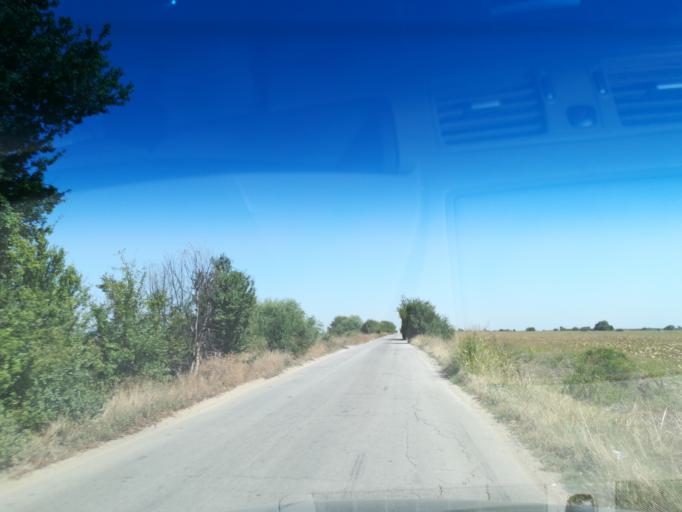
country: BG
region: Plovdiv
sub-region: Obshtina Suedinenie
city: Suedinenie
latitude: 42.2514
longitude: 24.4676
